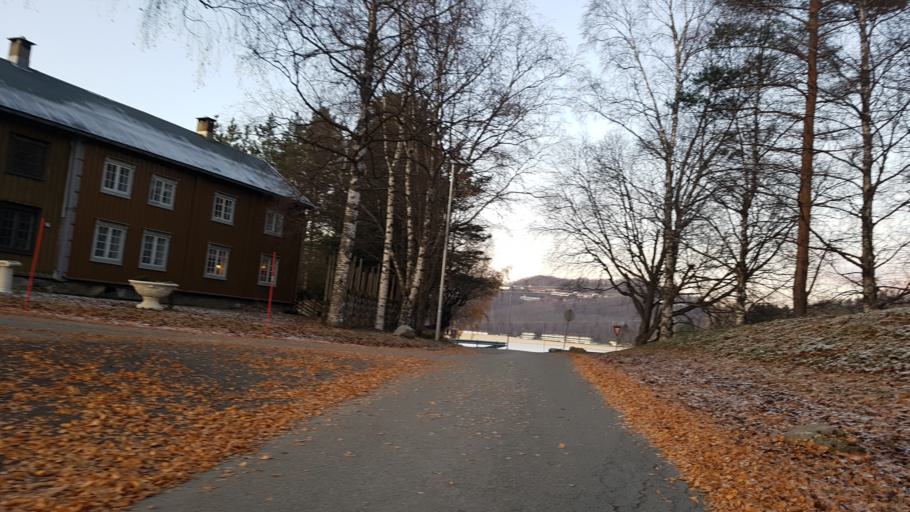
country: NO
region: Sor-Trondelag
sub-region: Melhus
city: Melhus
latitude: 63.2773
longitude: 10.2911
